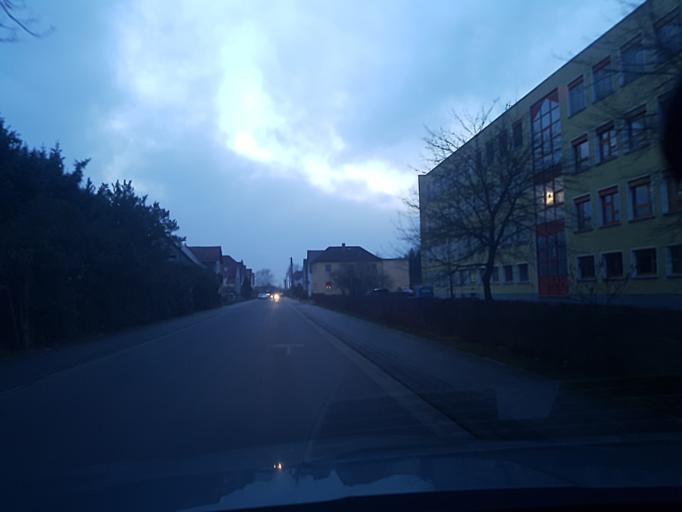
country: DE
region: Brandenburg
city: Doberlug-Kirchhain
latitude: 51.6085
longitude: 13.5513
